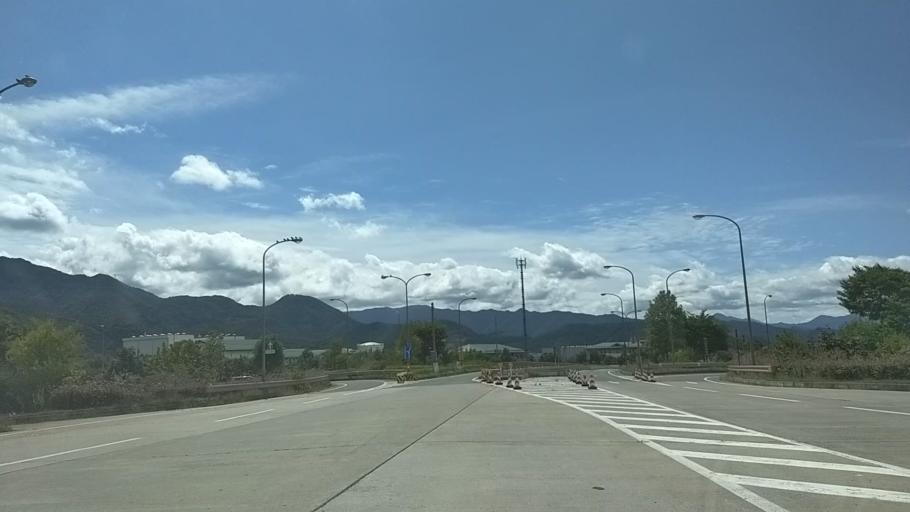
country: JP
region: Nagano
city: Nagano-shi
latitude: 36.6143
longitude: 138.2226
